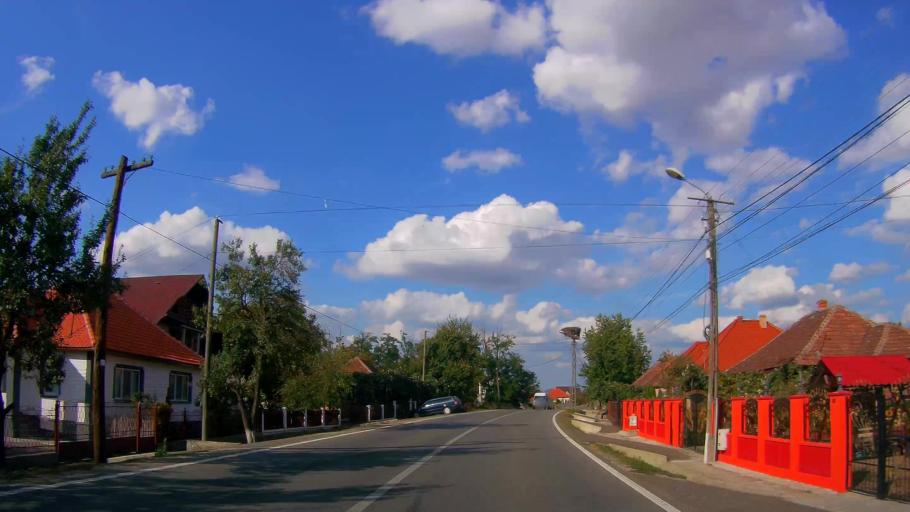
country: RO
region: Satu Mare
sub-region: Comuna Turulung
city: Draguseni
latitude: 47.9103
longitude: 23.0771
